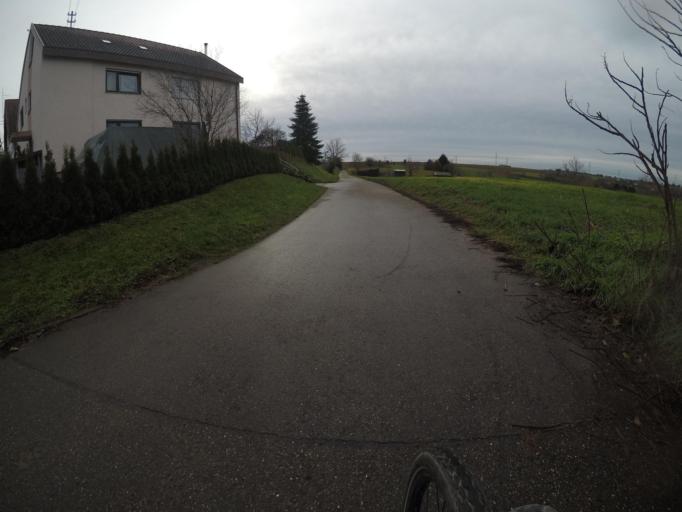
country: DE
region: Baden-Wuerttemberg
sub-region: Regierungsbezirk Stuttgart
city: Schwaikheim
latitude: 48.8723
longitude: 9.3439
